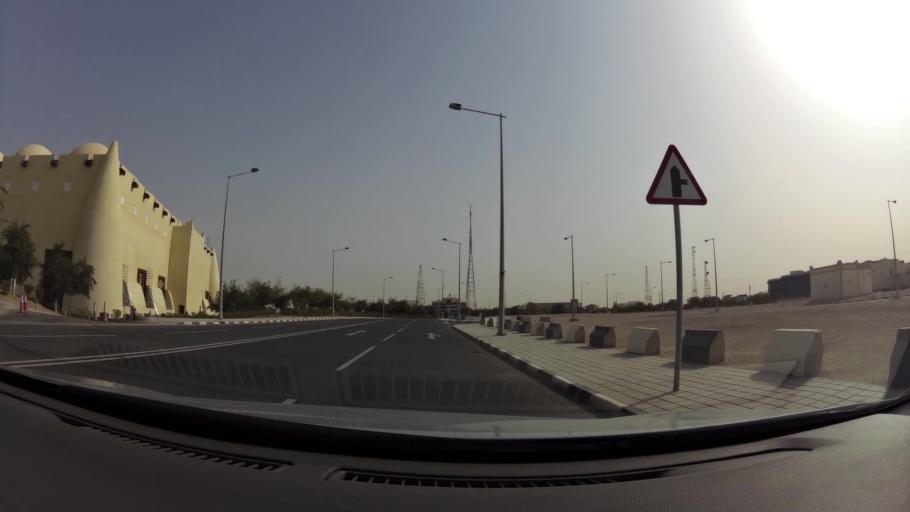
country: QA
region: Baladiyat ad Dawhah
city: Doha
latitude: 25.3179
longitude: 51.5037
